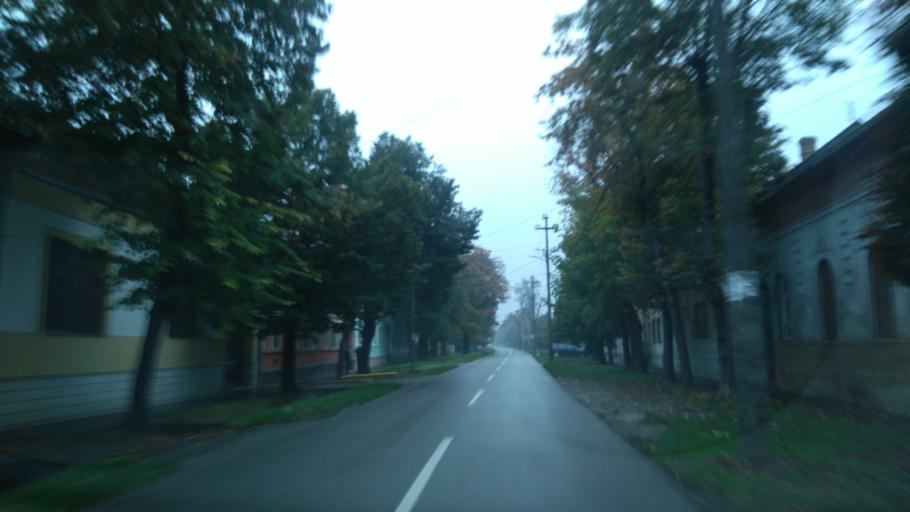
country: RS
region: Autonomna Pokrajina Vojvodina
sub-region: Juznobacki Okrug
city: Becej
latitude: 45.6119
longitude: 20.0472
